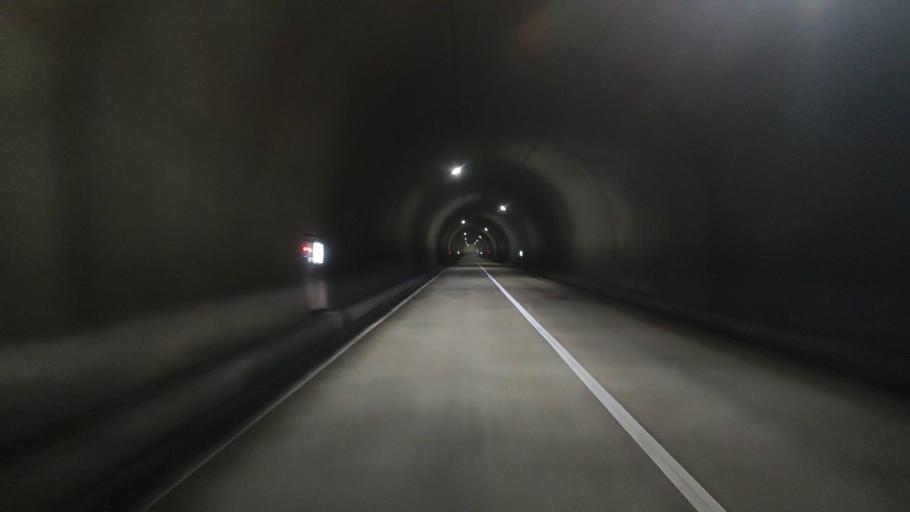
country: JP
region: Wakayama
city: Shingu
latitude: 33.8756
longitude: 135.8574
